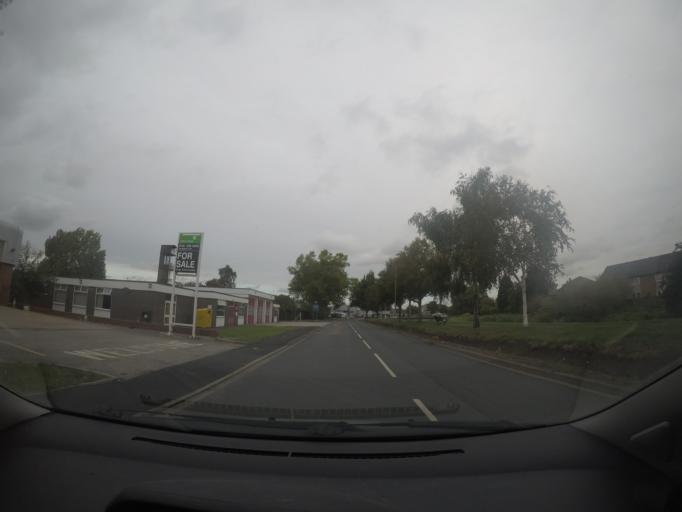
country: GB
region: England
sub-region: North Yorkshire
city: Selby
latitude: 53.7787
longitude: -1.0627
